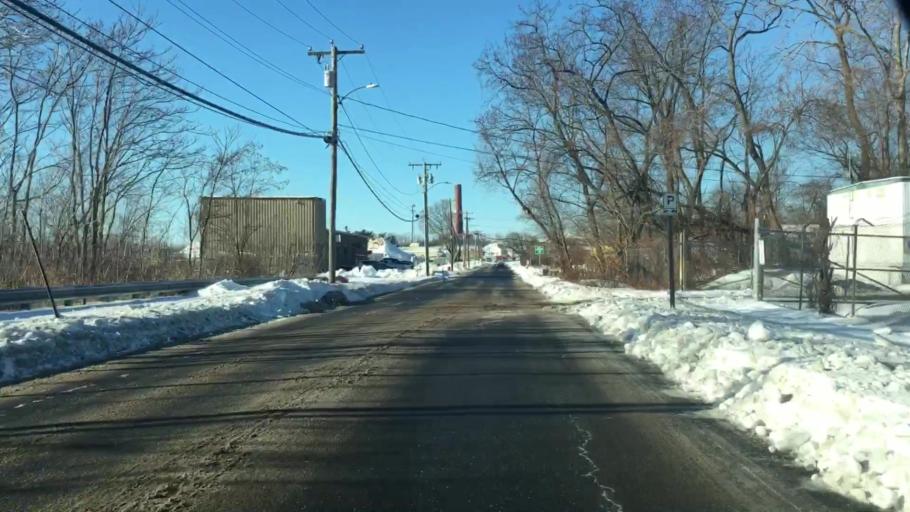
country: US
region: Connecticut
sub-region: Hartford County
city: Newington
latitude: 41.7343
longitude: -72.7141
